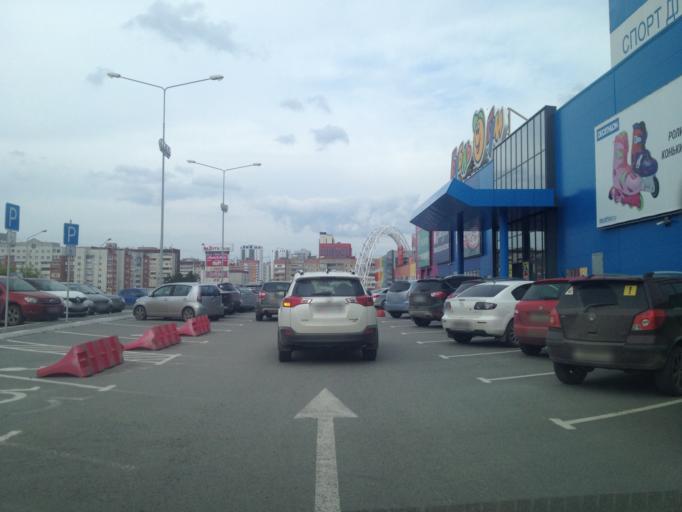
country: RU
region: Sverdlovsk
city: Shirokaya Rechka
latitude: 56.8165
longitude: 60.5356
